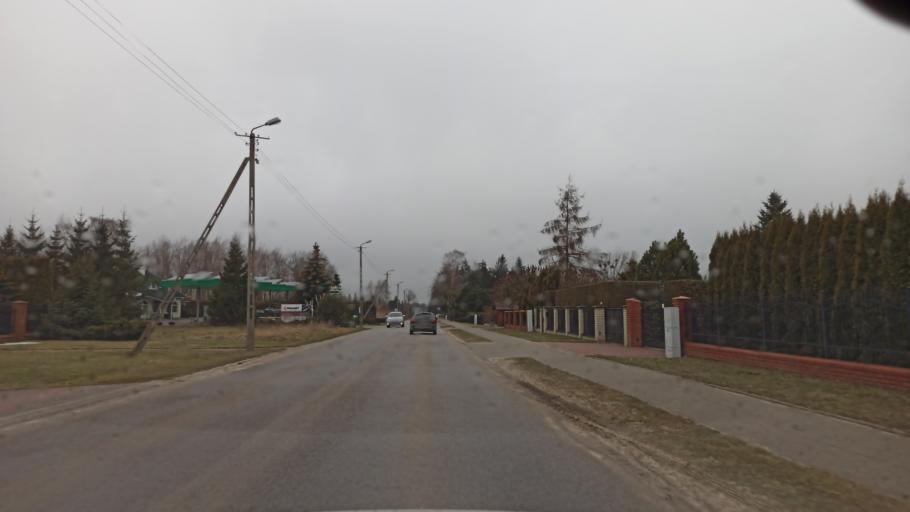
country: PL
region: Lublin Voivodeship
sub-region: Powiat lubelski
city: Bychawa
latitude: 51.0052
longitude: 22.5553
